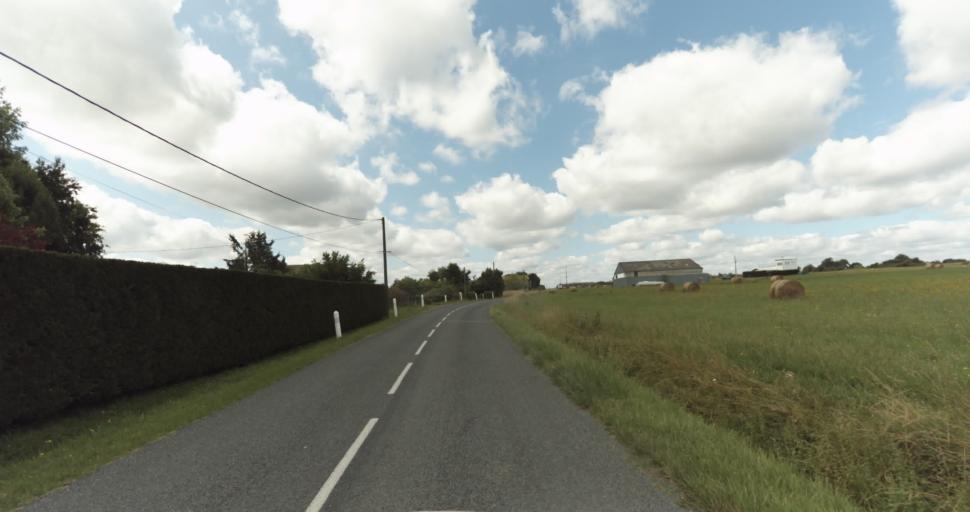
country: FR
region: Aquitaine
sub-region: Departement de la Gironde
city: Bazas
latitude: 44.4644
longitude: -0.1830
